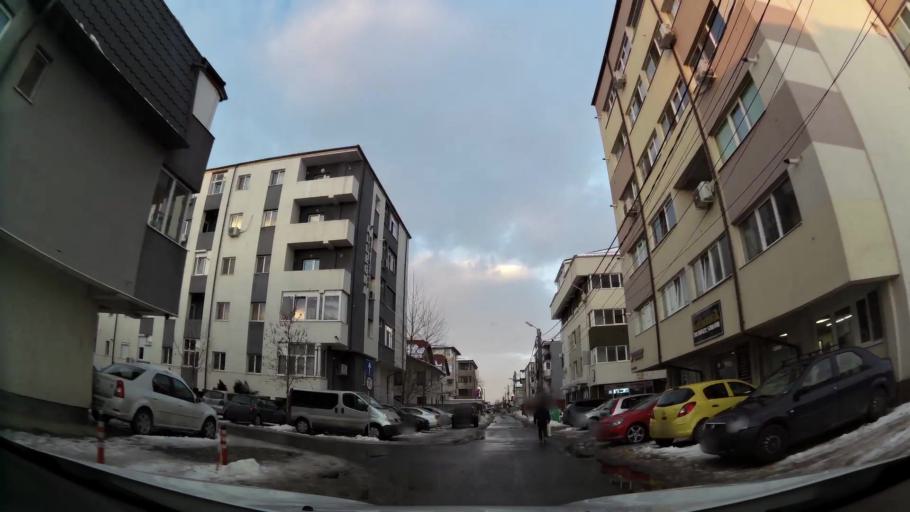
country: RO
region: Ilfov
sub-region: Comuna Popesti-Leordeni
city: Popesti-Leordeni
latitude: 44.3737
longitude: 26.1480
